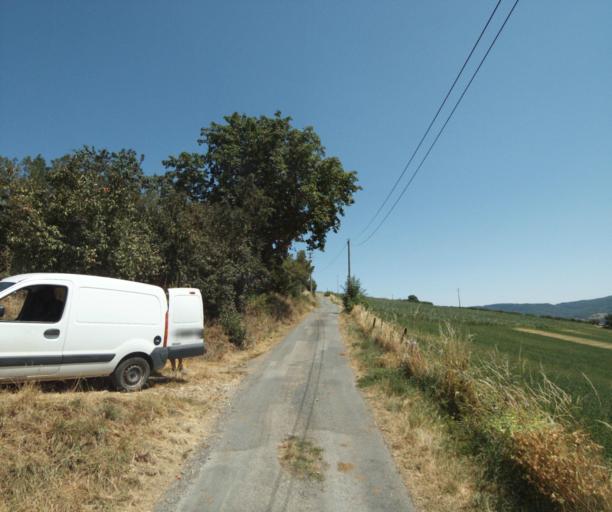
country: FR
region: Rhone-Alpes
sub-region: Departement du Rhone
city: Bessenay
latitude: 45.7757
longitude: 4.5315
